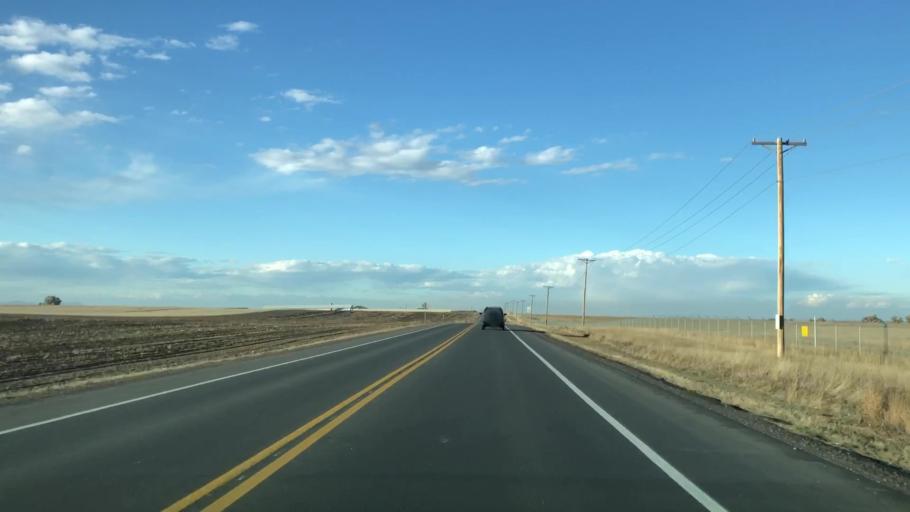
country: US
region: Colorado
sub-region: Larimer County
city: Loveland
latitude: 40.4511
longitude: -105.0205
